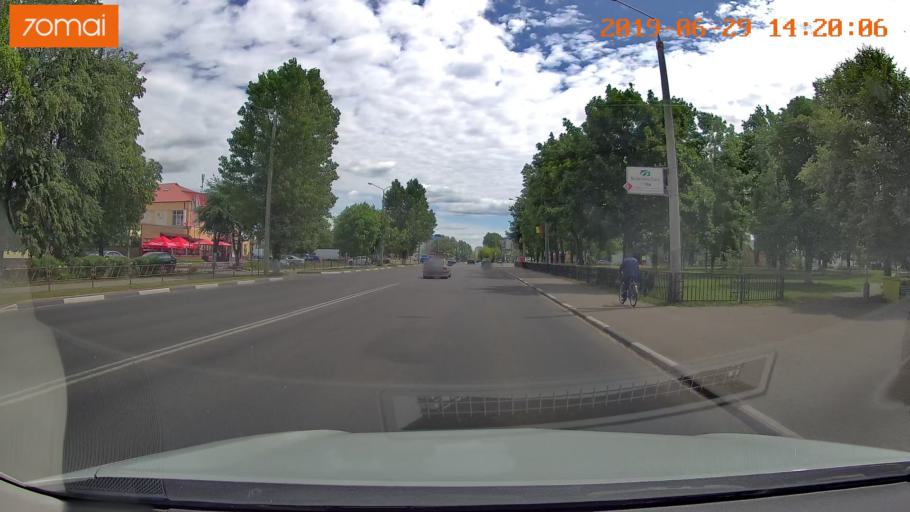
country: BY
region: Minsk
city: Salihorsk
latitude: 52.7943
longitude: 27.5416
